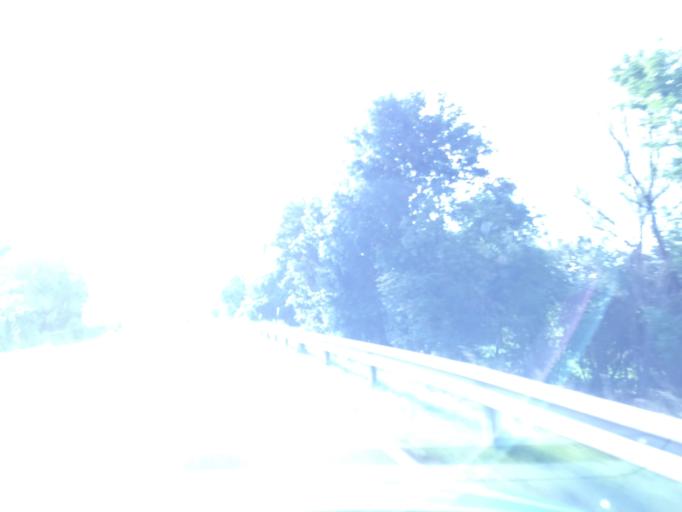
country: DE
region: Bavaria
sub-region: Swabia
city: Holzheim
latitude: 48.3688
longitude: 10.0623
